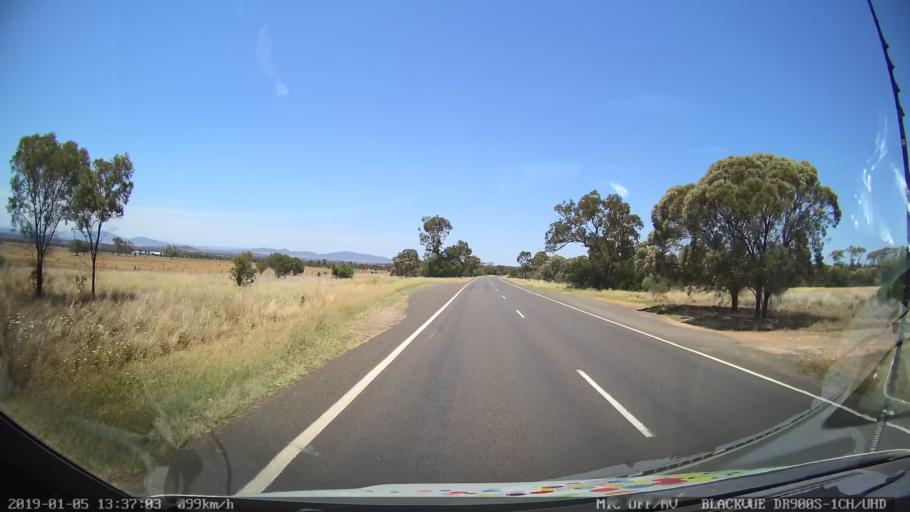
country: AU
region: New South Wales
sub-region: Gunnedah
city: Gunnedah
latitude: -30.9822
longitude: 150.1749
